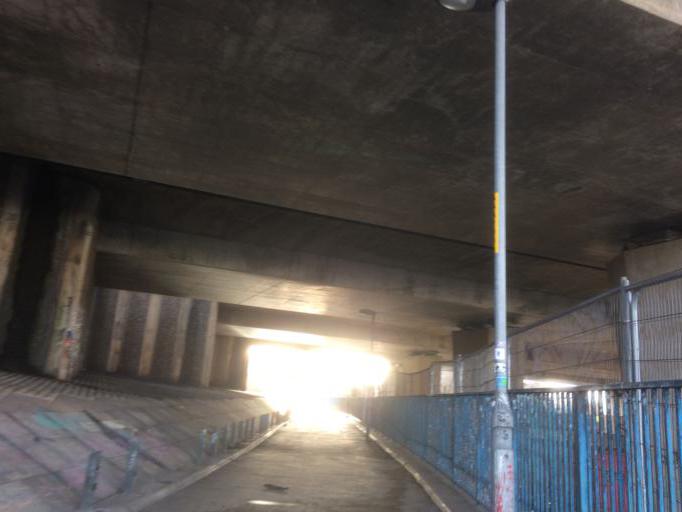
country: GB
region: Scotland
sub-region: Glasgow City
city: Glasgow
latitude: 55.8506
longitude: -4.2768
